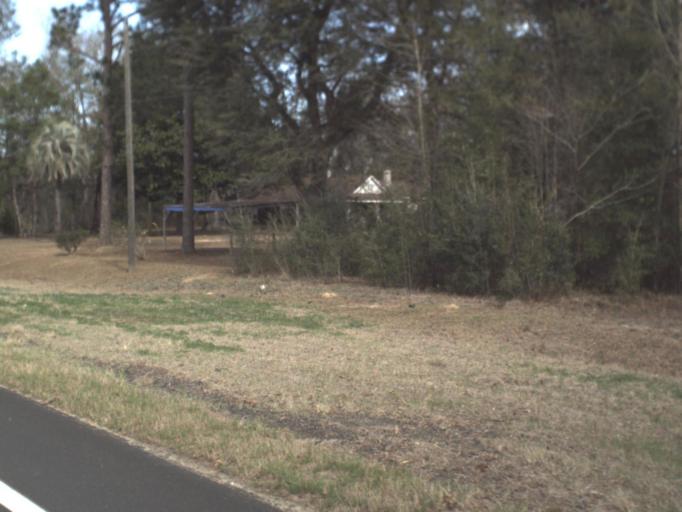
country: US
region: Florida
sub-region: Washington County
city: Chipley
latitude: 30.6712
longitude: -85.3936
